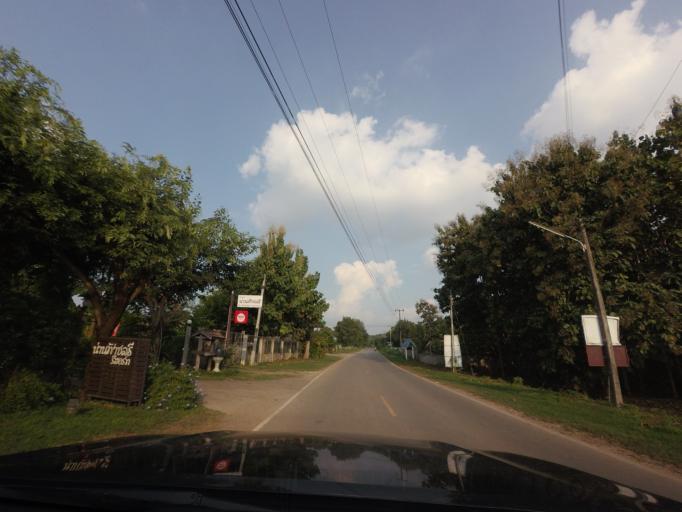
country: TH
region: Nan
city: Nan
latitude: 18.7743
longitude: 100.7394
